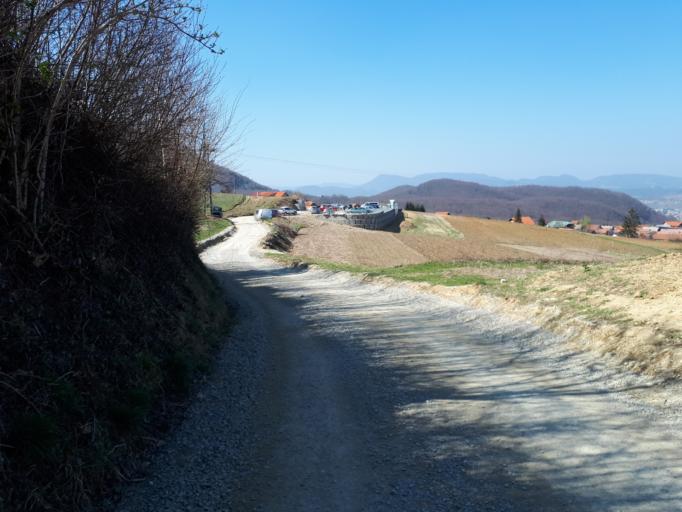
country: HR
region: Varazdinska
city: Ivanec
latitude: 46.1962
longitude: 16.1403
